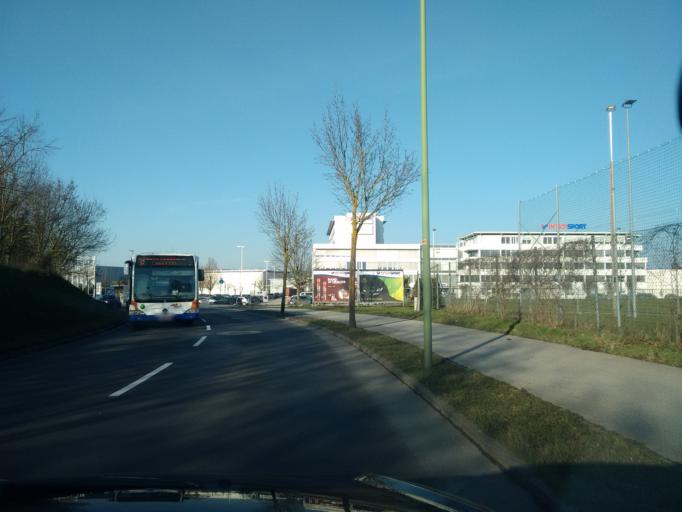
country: AT
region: Upper Austria
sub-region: Wels Stadt
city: Wels
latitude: 48.1751
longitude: 14.0431
